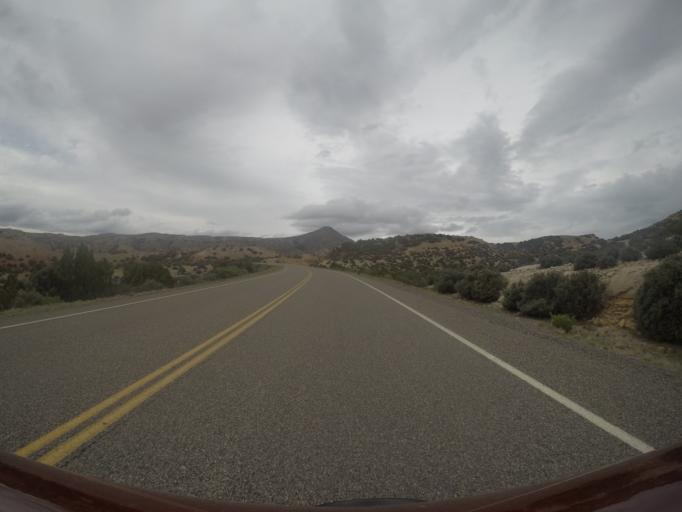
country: US
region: Wyoming
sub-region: Big Horn County
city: Lovell
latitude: 45.0080
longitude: -108.2684
